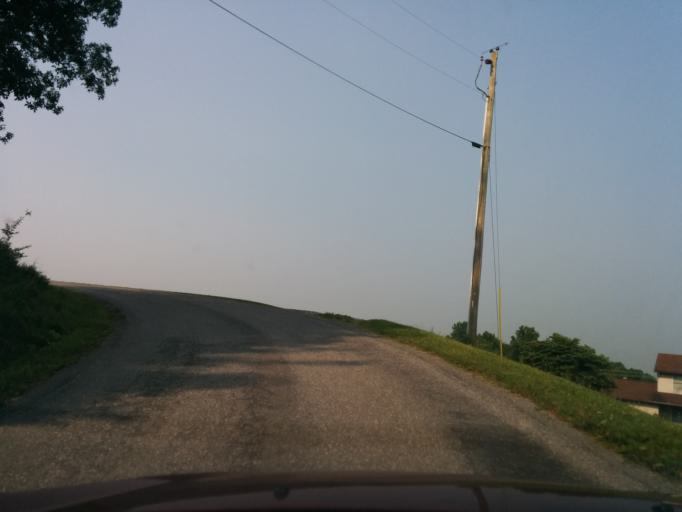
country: US
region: Virginia
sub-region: City of Lexington
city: Lexington
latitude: 37.7559
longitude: -79.4403
